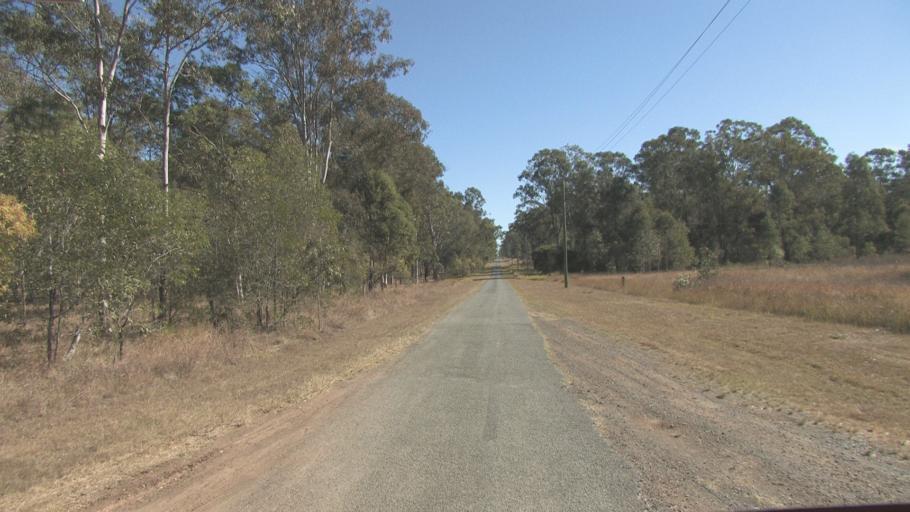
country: AU
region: Queensland
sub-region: Logan
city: North Maclean
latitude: -27.8223
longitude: 152.9919
